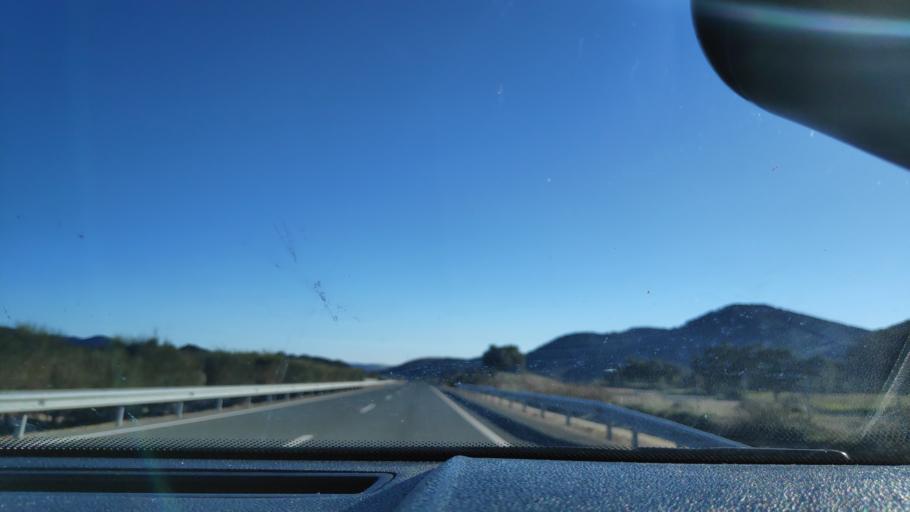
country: ES
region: Extremadura
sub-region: Provincia de Badajoz
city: Monesterio
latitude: 38.0605
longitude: -6.2415
